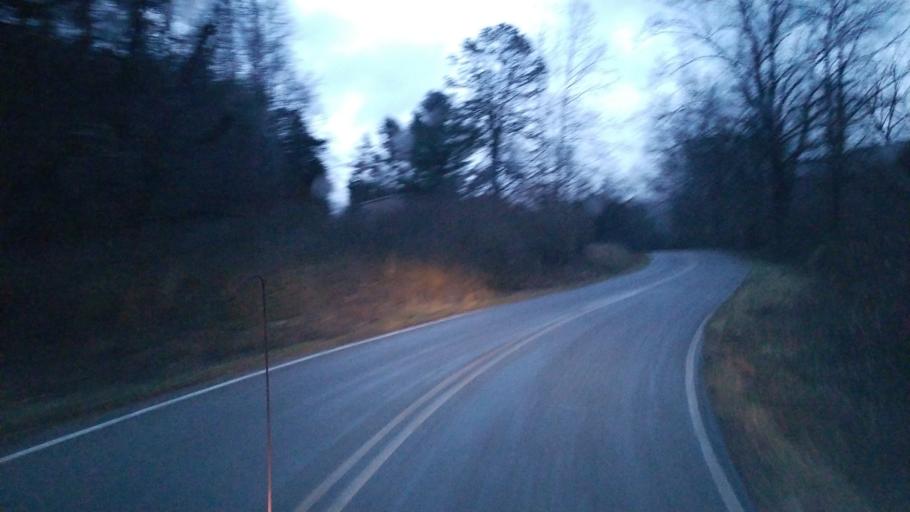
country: US
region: Virginia
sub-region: Pulaski County
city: Pulaski
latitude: 37.1471
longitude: -80.8319
